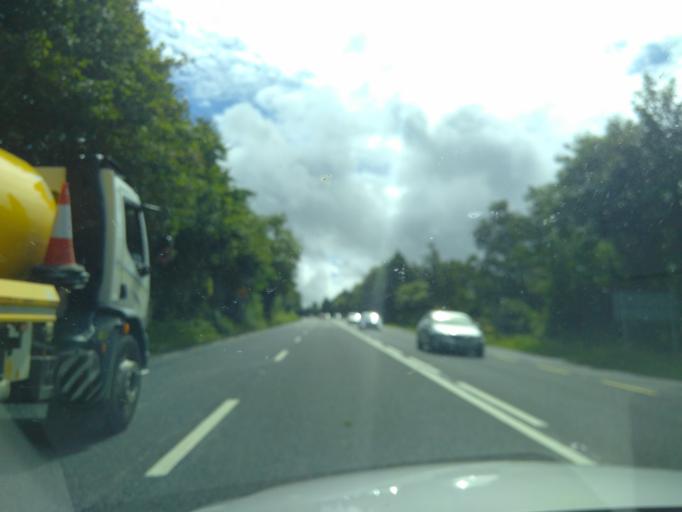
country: IE
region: Ulster
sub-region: County Donegal
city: Letterkenny
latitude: 54.9352
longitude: -7.6960
